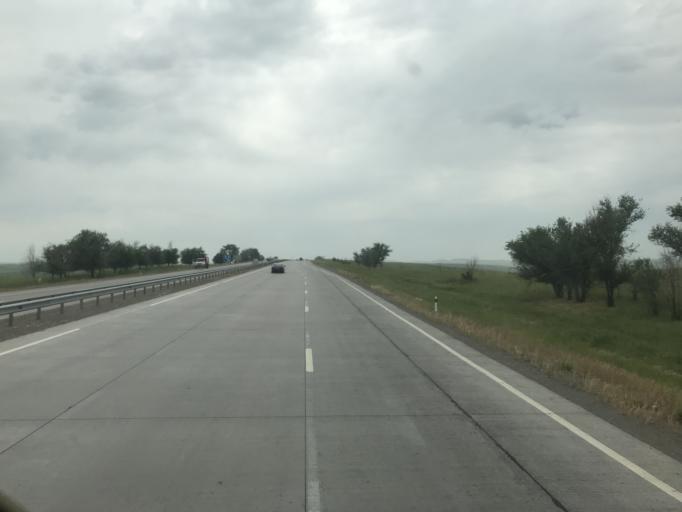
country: KZ
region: Ongtustik Qazaqstan
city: Shymkent
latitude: 42.1936
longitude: 69.5064
